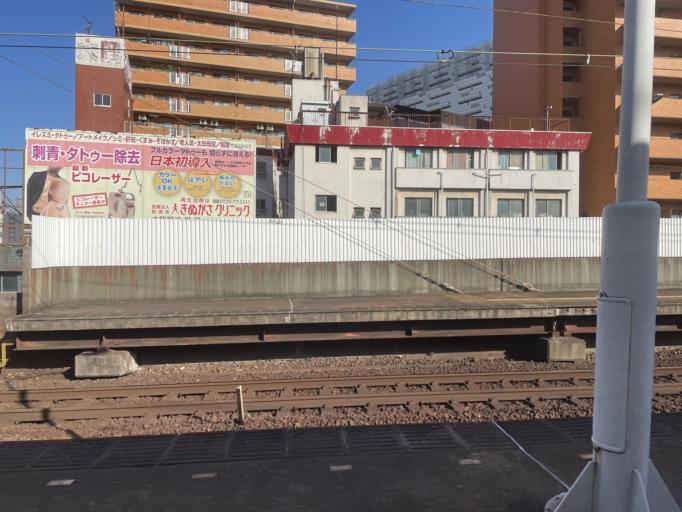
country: JP
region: Osaka
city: Osaka-shi
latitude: 34.6515
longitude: 135.5006
